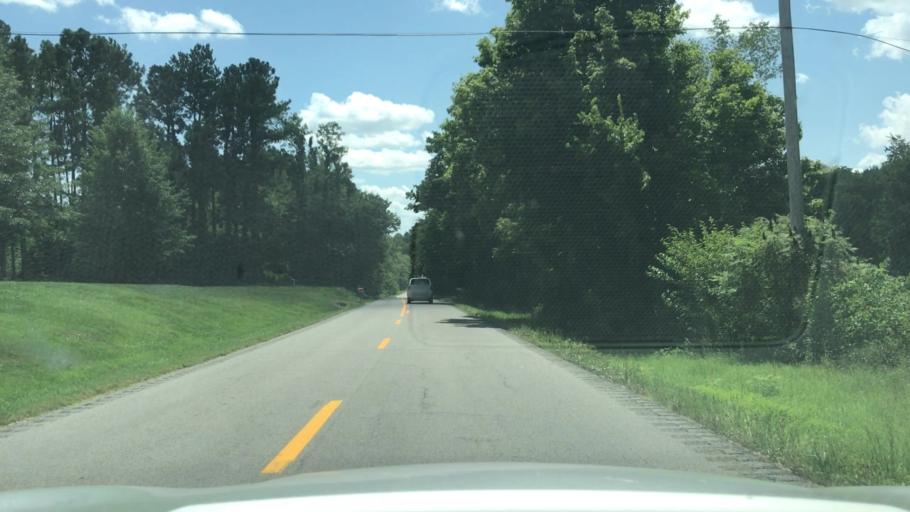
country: US
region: Kentucky
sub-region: Christian County
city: Hopkinsville
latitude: 36.9116
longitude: -87.4430
